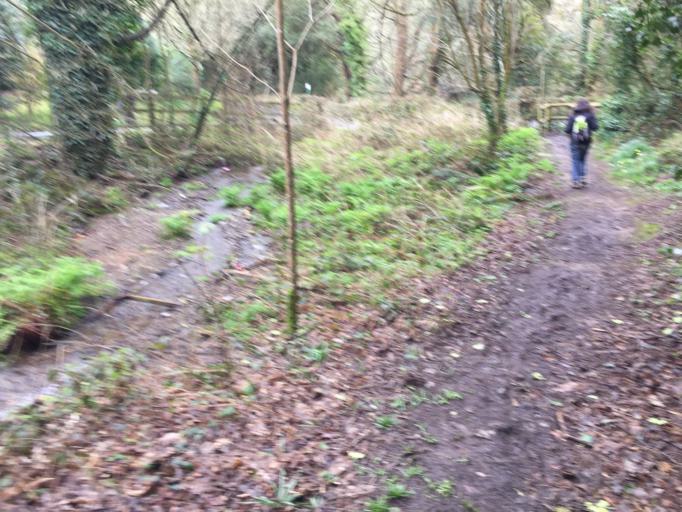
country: JE
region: St Helier
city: Saint Helier
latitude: 49.2186
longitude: -2.1341
